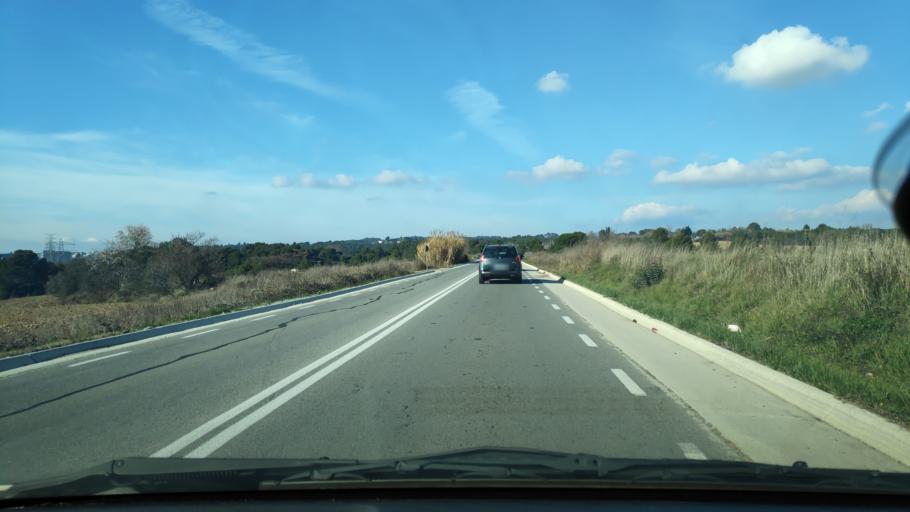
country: ES
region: Catalonia
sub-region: Provincia de Barcelona
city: Sant Cugat del Valles
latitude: 41.4844
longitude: 2.0979
